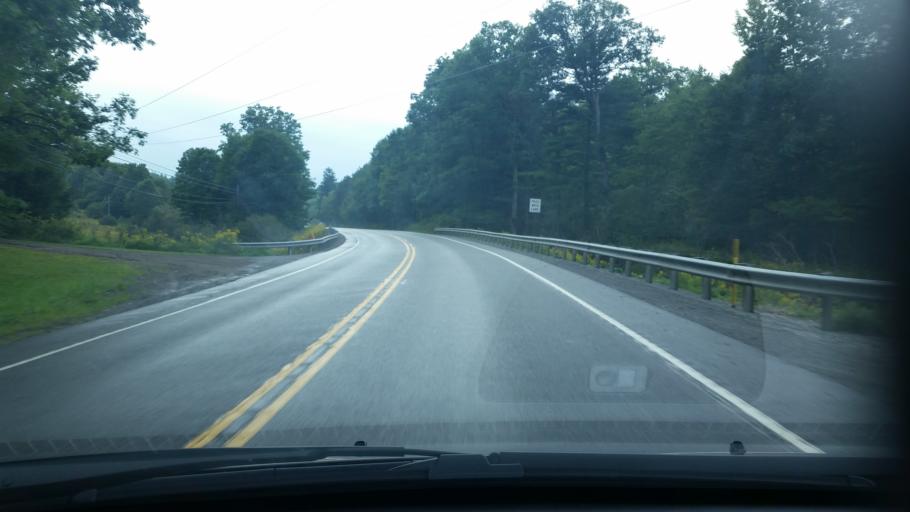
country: US
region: Pennsylvania
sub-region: Clearfield County
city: Shiloh
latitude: 41.0862
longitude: -78.2629
